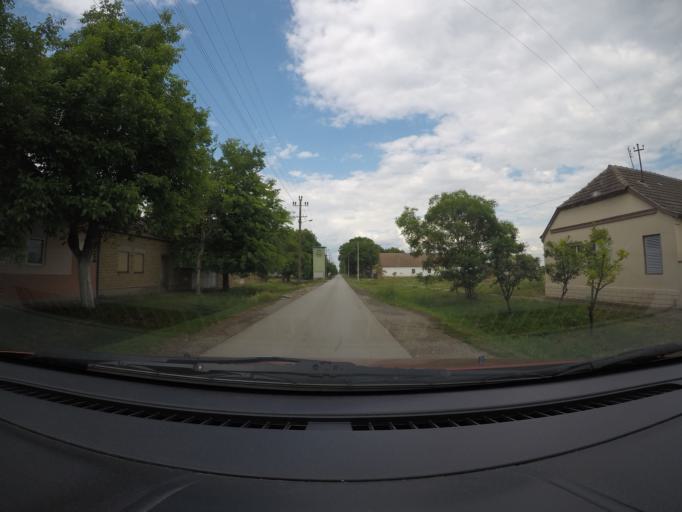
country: RS
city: Begejci
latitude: 45.4999
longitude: 20.5961
